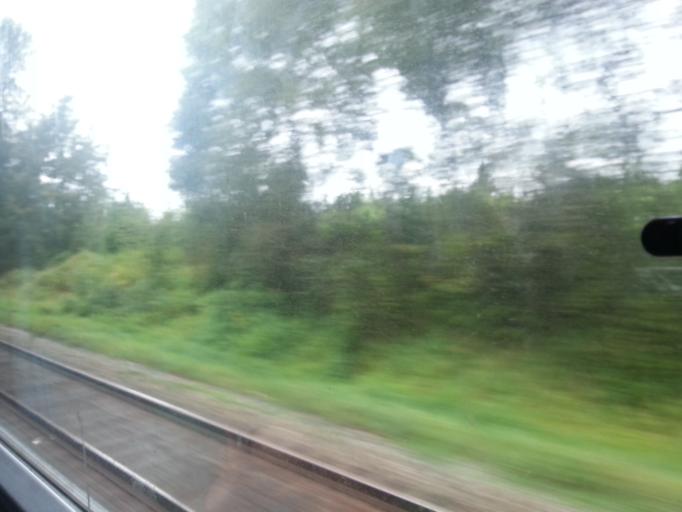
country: CA
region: British Columbia
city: Walnut Grove
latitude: 49.1776
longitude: -122.6201
